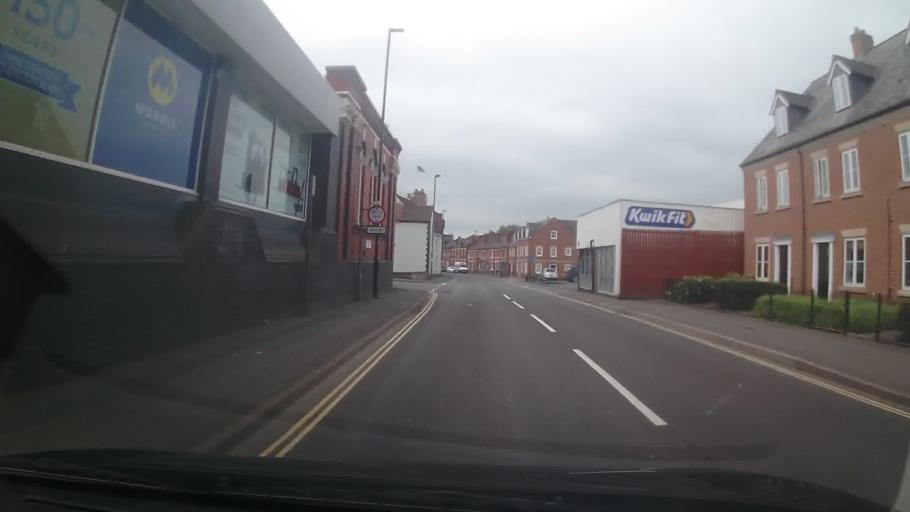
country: GB
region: England
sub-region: Shropshire
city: Shrewsbury
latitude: 52.7149
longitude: -2.7484
